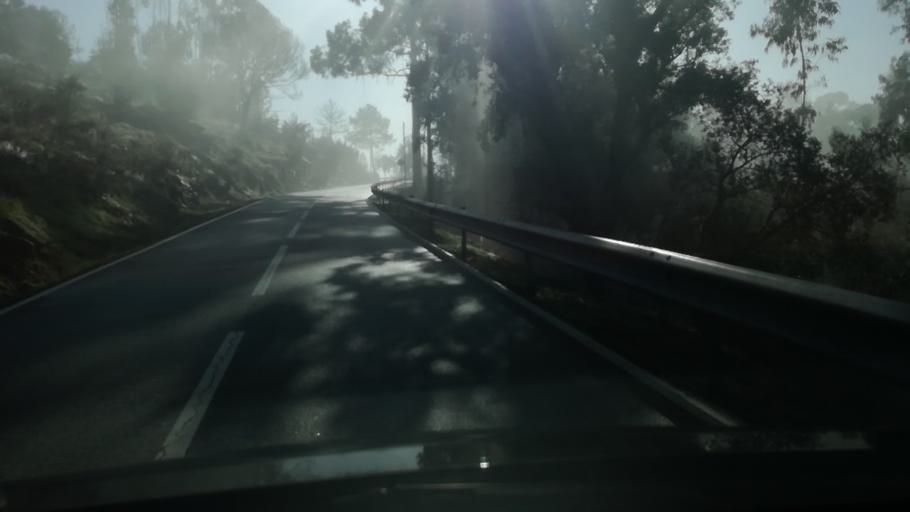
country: PT
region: Braga
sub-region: Guimaraes
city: Ponte
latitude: 41.5277
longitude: -8.3192
